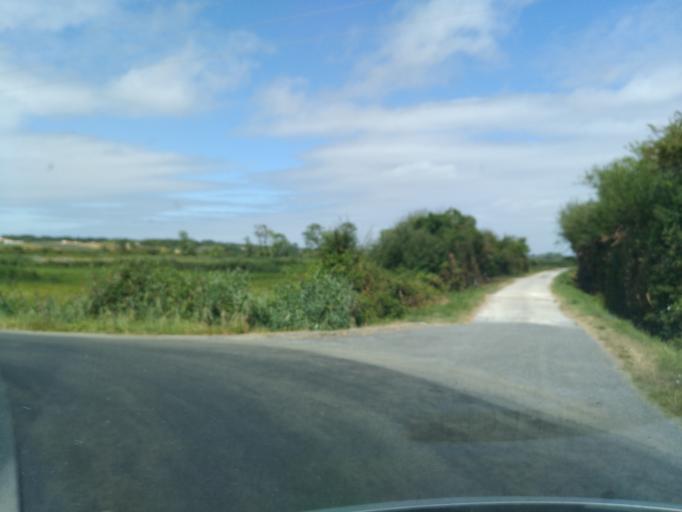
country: FR
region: Poitou-Charentes
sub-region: Departement de la Charente-Maritime
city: Breuillet
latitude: 45.6829
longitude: -1.0809
